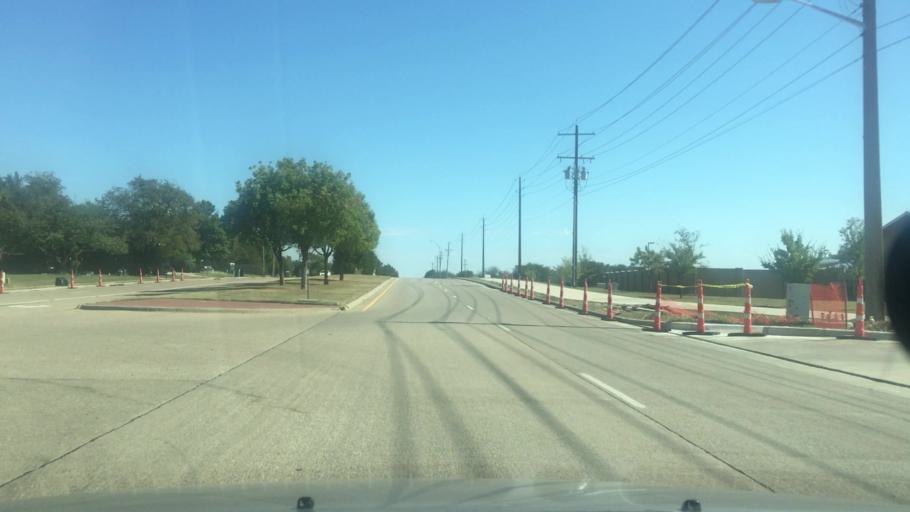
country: US
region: Texas
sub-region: Denton County
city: Denton
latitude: 33.2483
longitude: -97.1480
